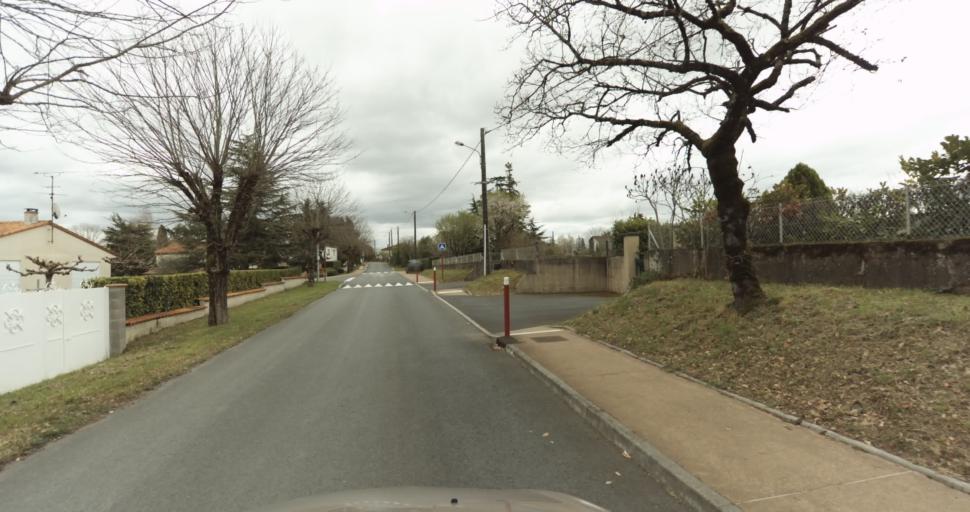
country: FR
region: Midi-Pyrenees
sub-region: Departement du Tarn
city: Puygouzon
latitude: 43.8954
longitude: 2.1742
